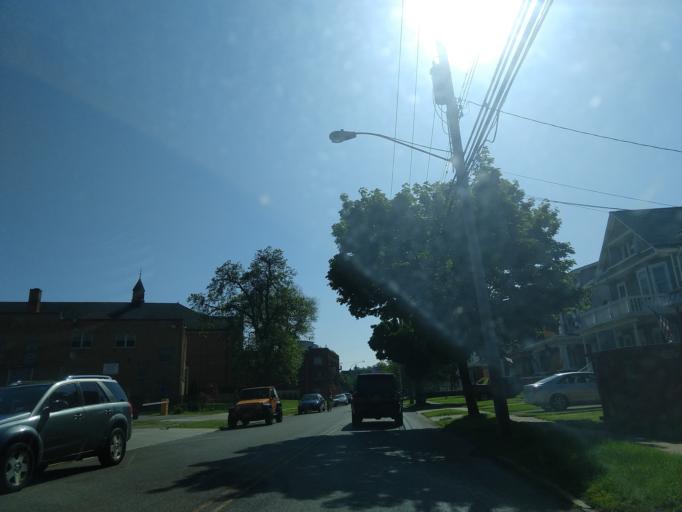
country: US
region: New York
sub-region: Erie County
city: West Seneca
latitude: 42.8589
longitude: -78.8114
